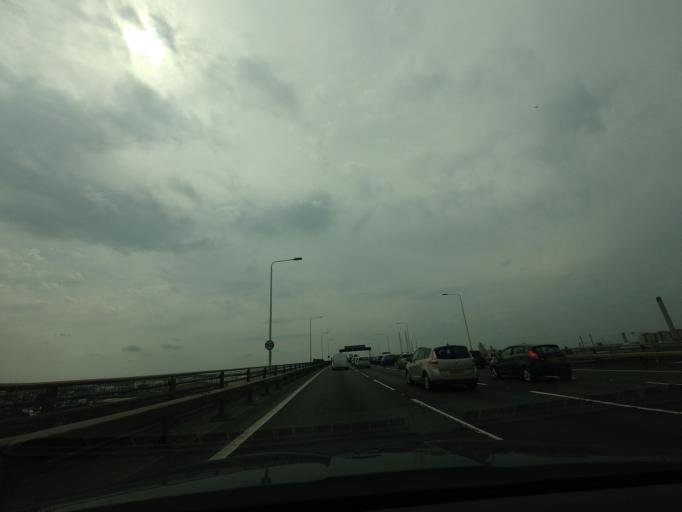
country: GB
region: England
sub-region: Kent
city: West Thurrock
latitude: 51.4756
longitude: 0.2665
